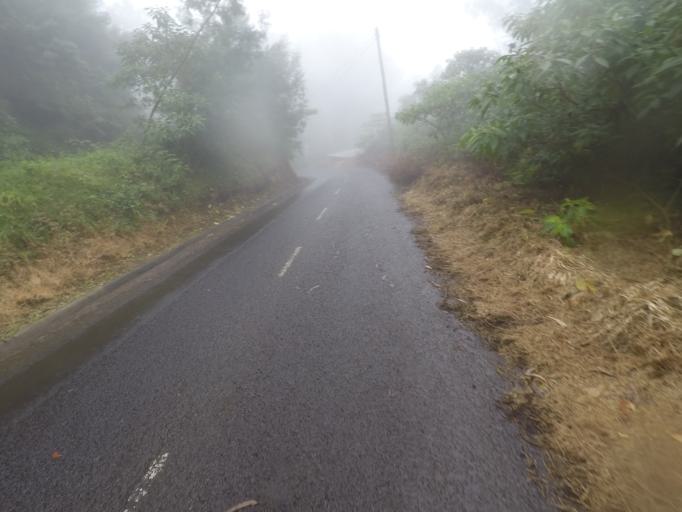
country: PT
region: Madeira
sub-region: Santa Cruz
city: Santa Cruz
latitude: 32.7465
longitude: -16.8238
